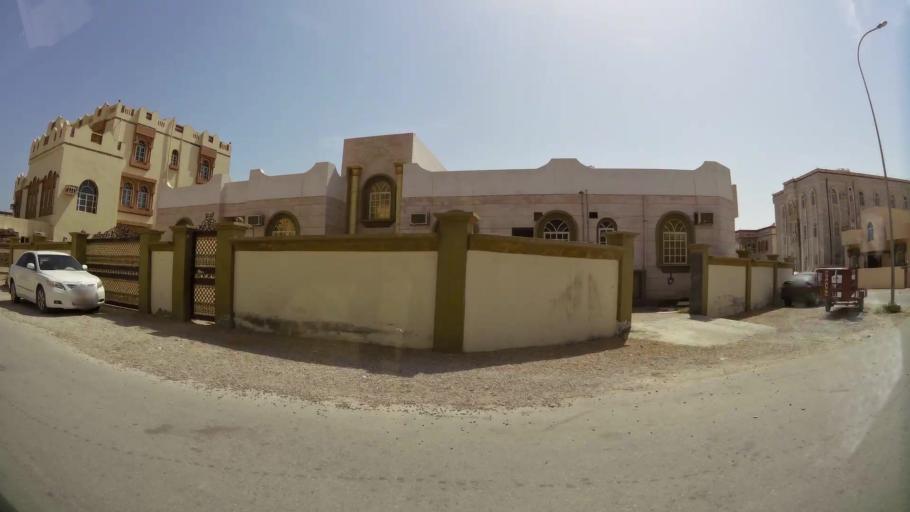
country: OM
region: Zufar
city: Salalah
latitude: 17.0452
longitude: 54.1601
